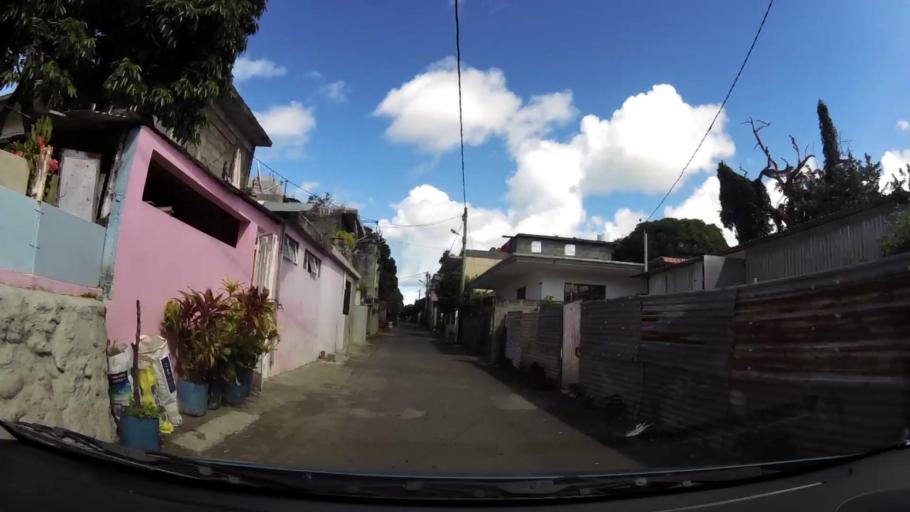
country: MU
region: Grand Port
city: Plaine Magnien
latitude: -20.4322
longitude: 57.6648
